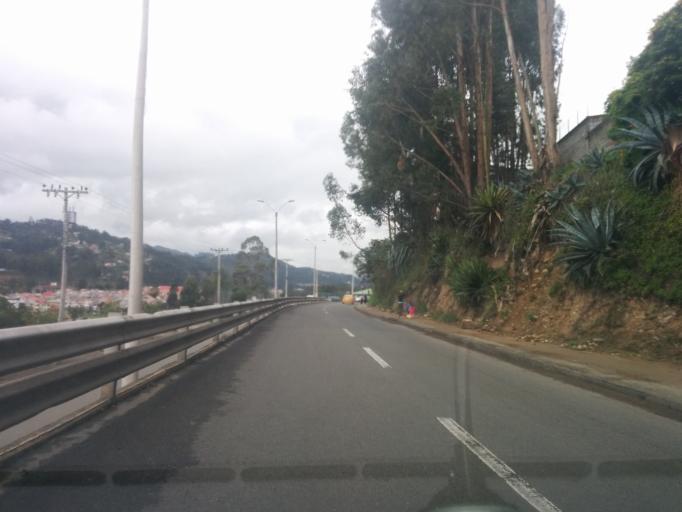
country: EC
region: Azuay
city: Cuenca
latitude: -2.8958
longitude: -78.9738
